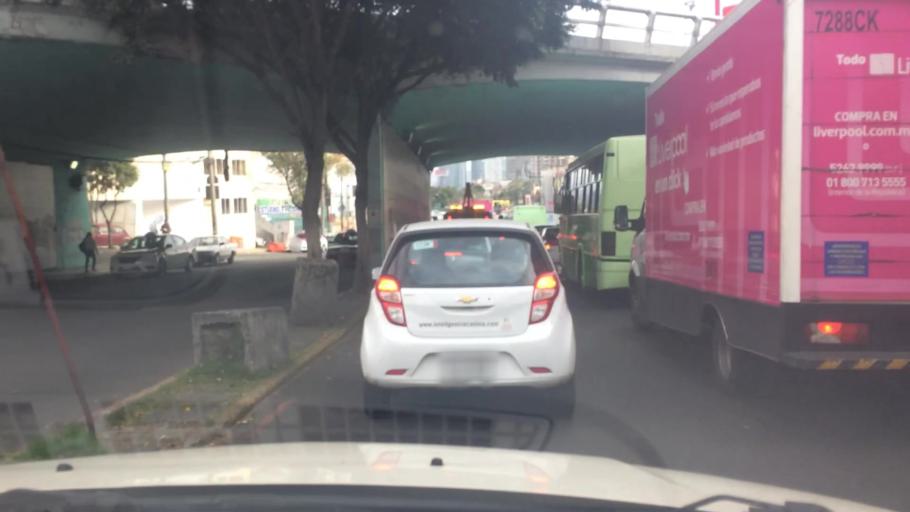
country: MX
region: Mexico City
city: Polanco
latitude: 19.3994
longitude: -99.1890
